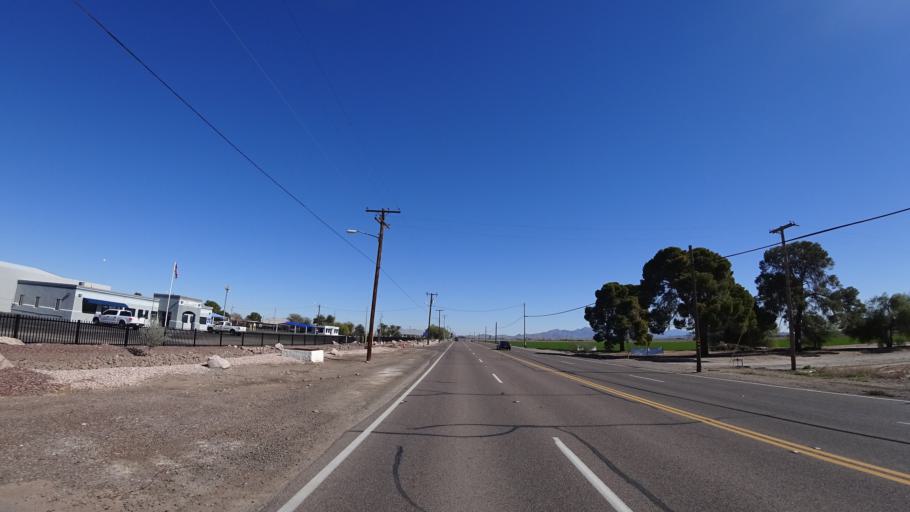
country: US
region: Arizona
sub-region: Maricopa County
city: Buckeye
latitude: 33.3776
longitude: -112.5559
